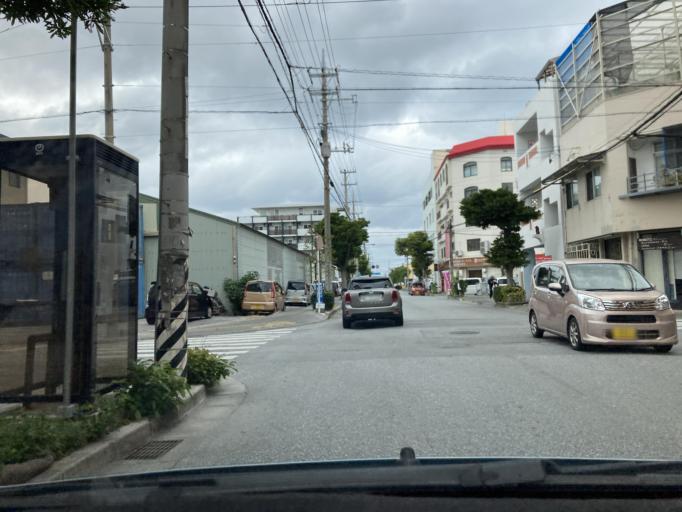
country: JP
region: Okinawa
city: Naha-shi
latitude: 26.2150
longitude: 127.6705
